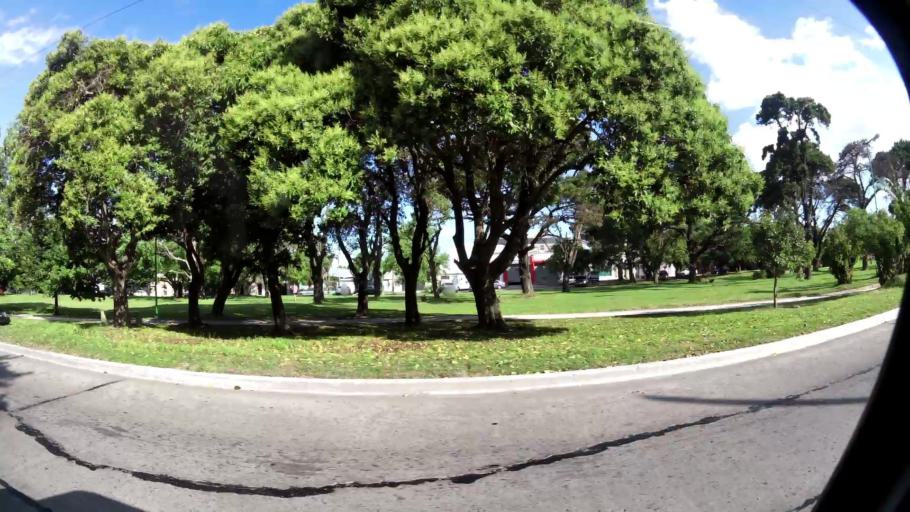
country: AR
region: Buenos Aires
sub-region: Partido de La Plata
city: La Plata
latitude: -34.8912
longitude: -57.9595
